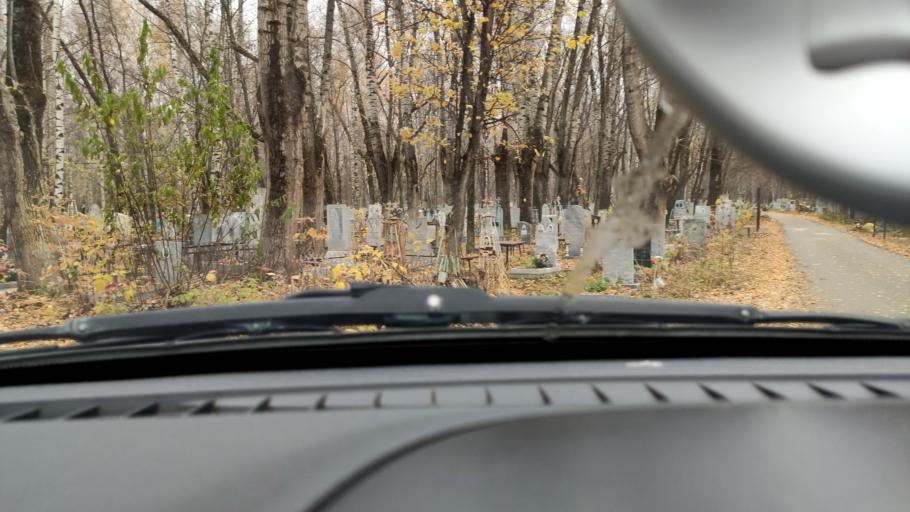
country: RU
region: Perm
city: Perm
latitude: 57.9892
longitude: 56.2848
